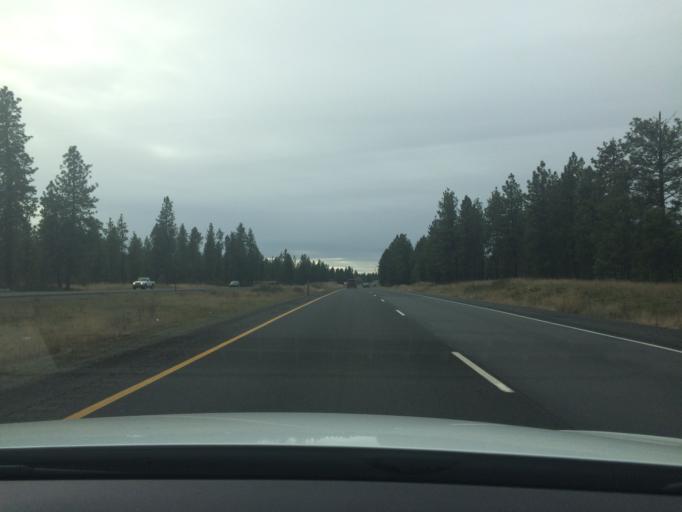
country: US
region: Washington
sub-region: Spokane County
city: Medical Lake
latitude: 47.5176
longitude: -117.6723
